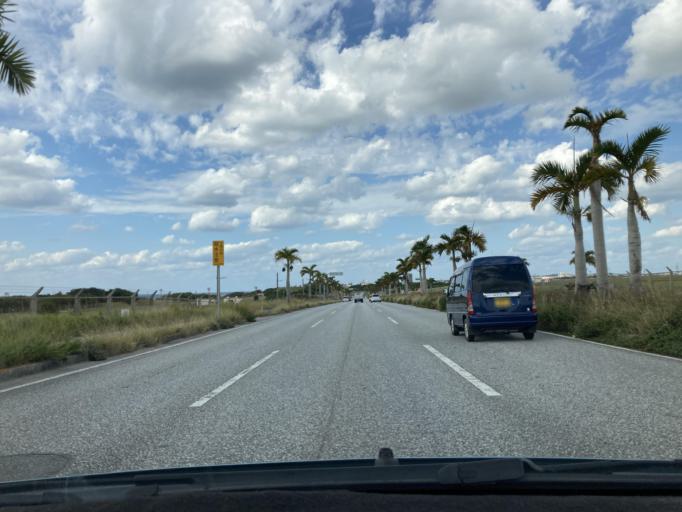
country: JP
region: Okinawa
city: Chatan
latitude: 26.3407
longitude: 127.7500
